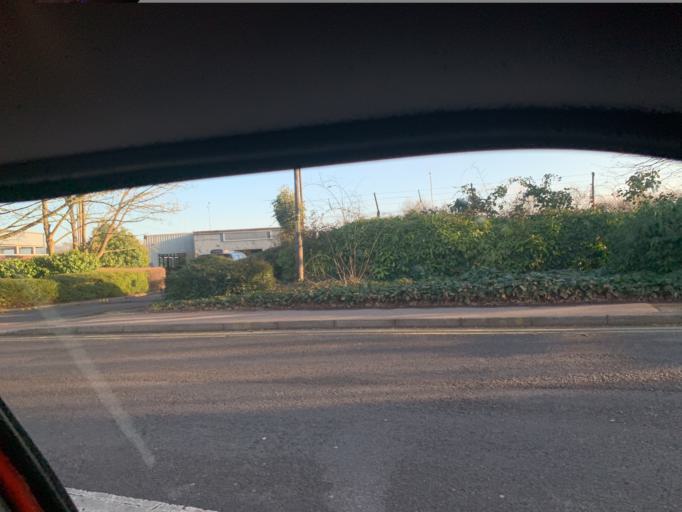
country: GB
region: England
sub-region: Surrey
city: Horley
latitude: 51.1553
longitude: -0.1569
